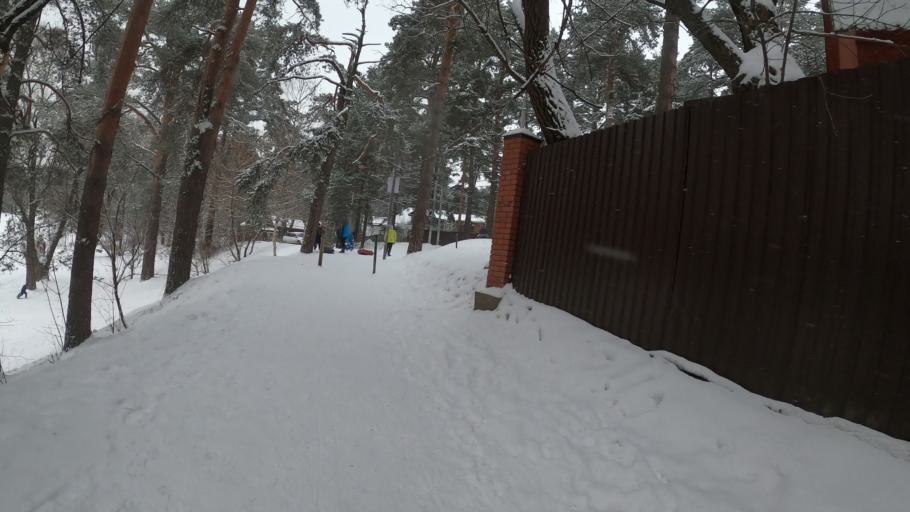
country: RU
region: Moskovskaya
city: Kratovo
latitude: 55.5897
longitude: 38.1588
